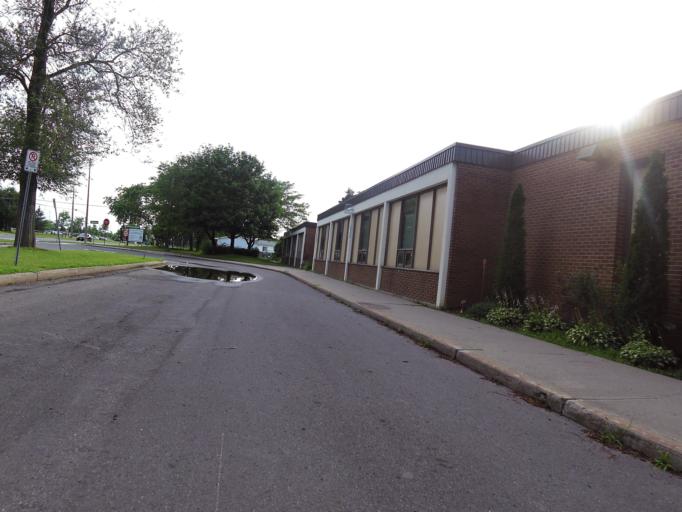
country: CA
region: Ontario
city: Bells Corners
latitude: 45.3278
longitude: -75.7685
